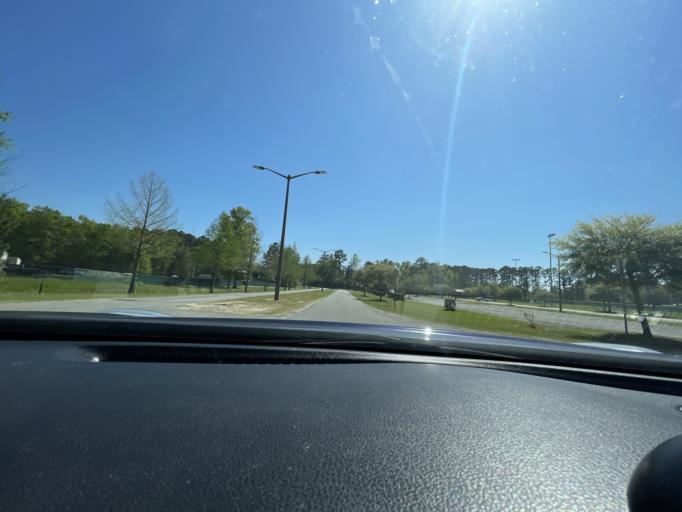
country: US
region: Georgia
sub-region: Chatham County
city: Pooler
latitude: 32.1326
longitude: -81.2627
